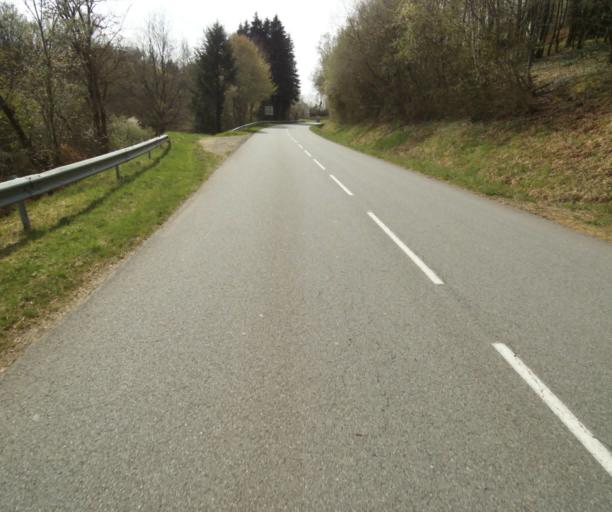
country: FR
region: Limousin
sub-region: Departement de la Correze
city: Naves
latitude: 45.3304
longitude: 1.7706
